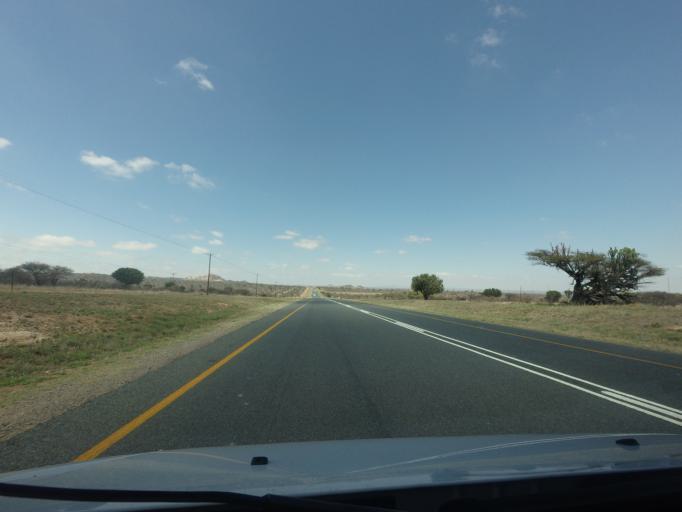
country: ZA
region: Limpopo
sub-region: Vhembe District Municipality
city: Louis Trichardt
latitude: -23.4058
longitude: 29.7573
